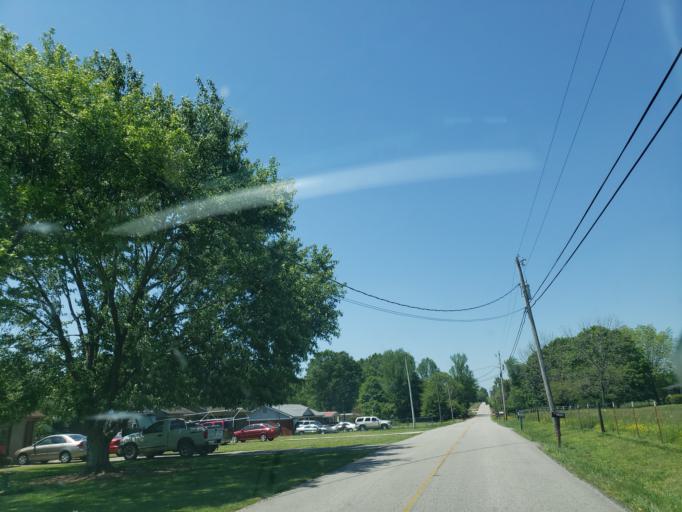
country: US
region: Alabama
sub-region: Madison County
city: Hazel Green
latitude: 34.9620
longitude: -86.6331
